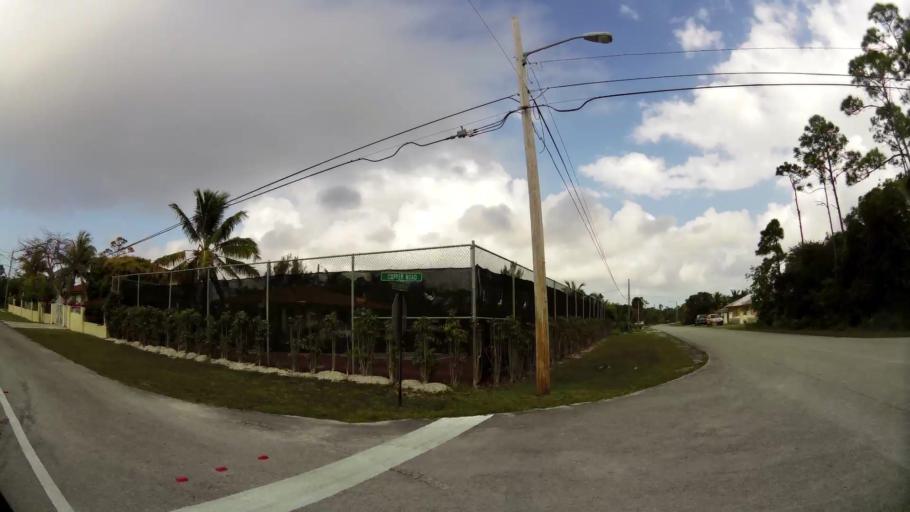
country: BS
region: Freeport
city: Lucaya
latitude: 26.5411
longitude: -78.5927
